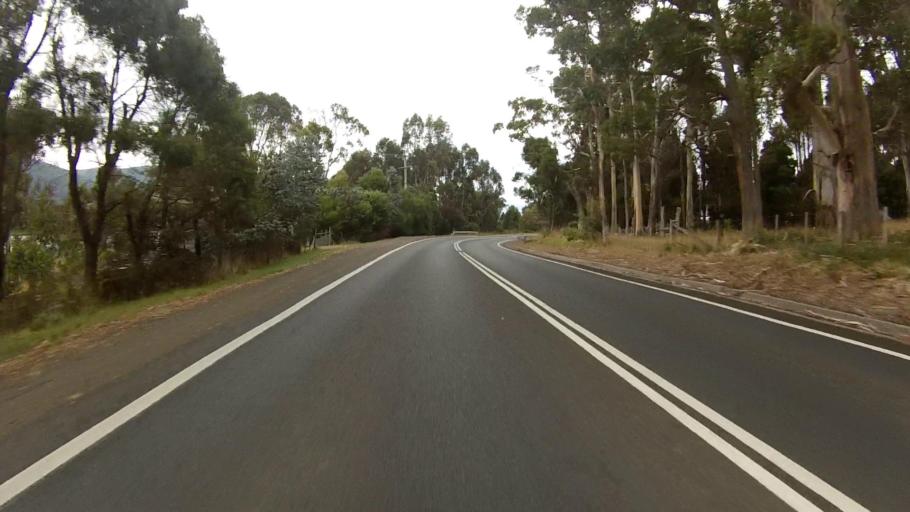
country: AU
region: Tasmania
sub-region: Huon Valley
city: Franklin
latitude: -43.0776
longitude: 147.0329
